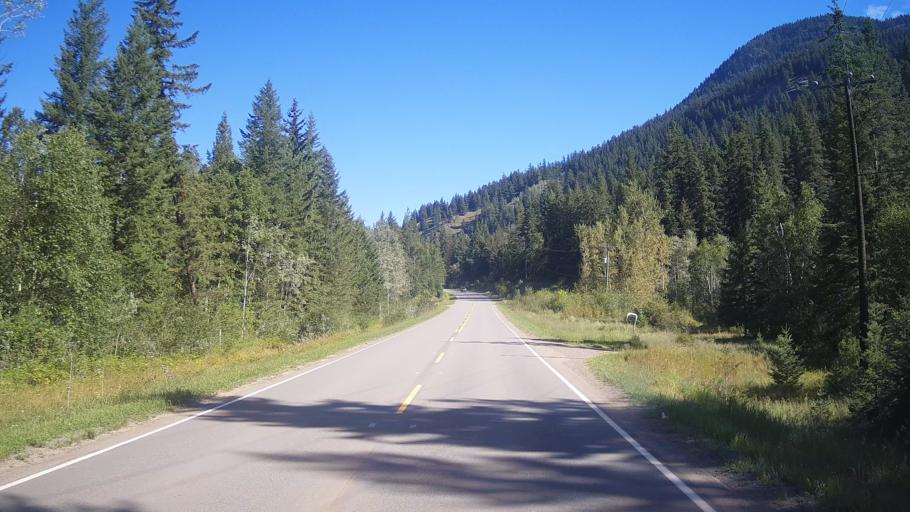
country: CA
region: British Columbia
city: Kamloops
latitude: 51.4443
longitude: -120.2123
